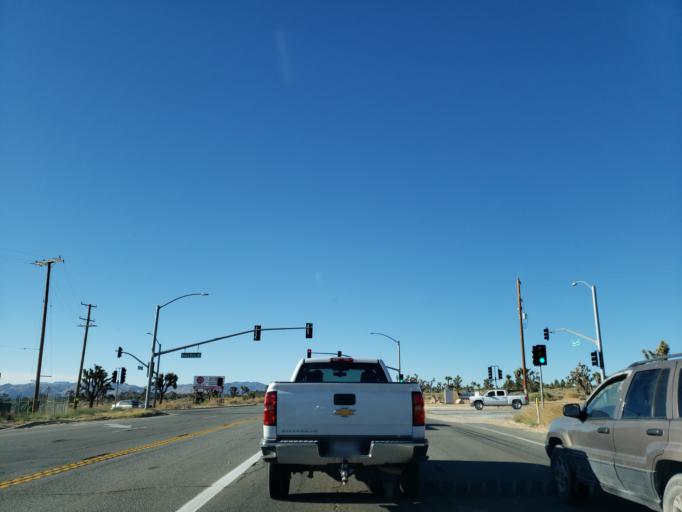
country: US
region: California
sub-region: San Bernardino County
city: Yucca Valley
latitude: 34.1648
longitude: -116.4228
